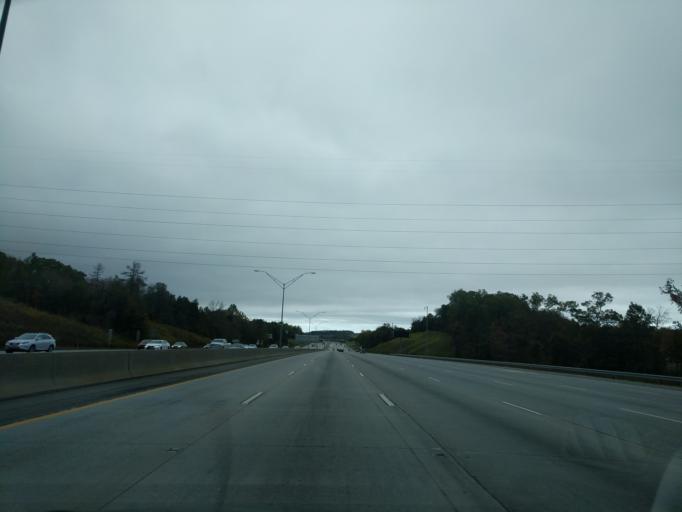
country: US
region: North Carolina
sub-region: Cabarrus County
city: Harrisburg
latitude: 35.3569
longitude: -80.7251
